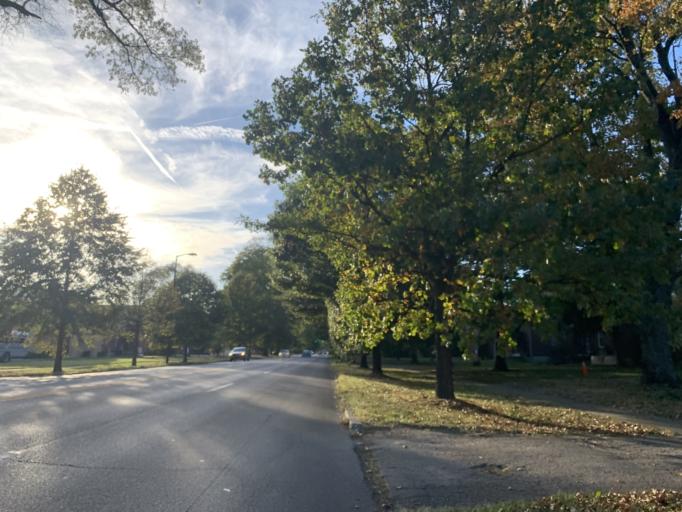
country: US
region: Kentucky
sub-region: Jefferson County
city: Shively
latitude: 38.2236
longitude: -85.7979
